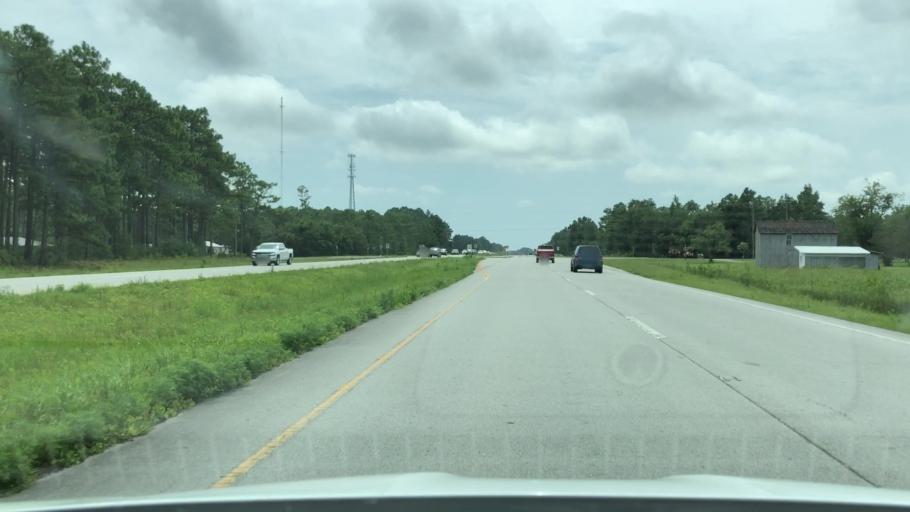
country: US
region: North Carolina
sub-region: Carteret County
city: Newport
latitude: 34.8068
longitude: -76.8792
